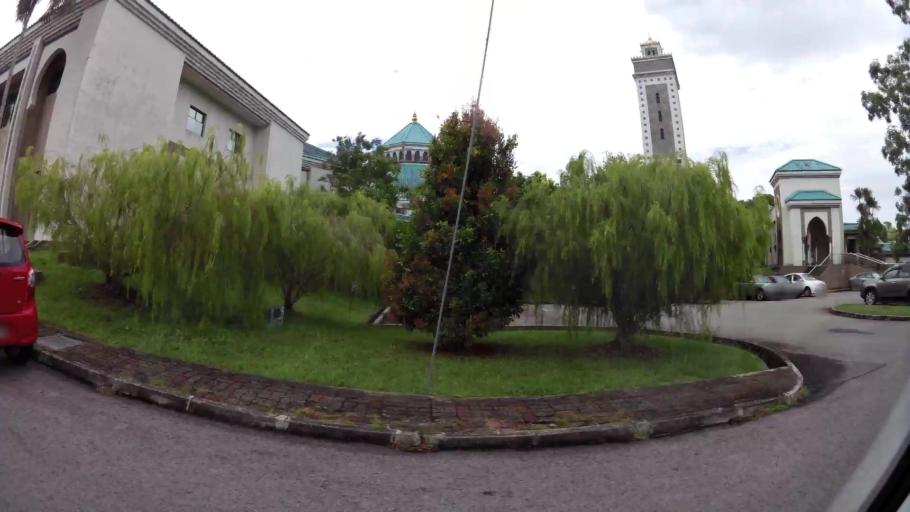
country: BN
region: Brunei and Muara
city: Bandar Seri Begawan
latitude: 4.8819
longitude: 114.9271
